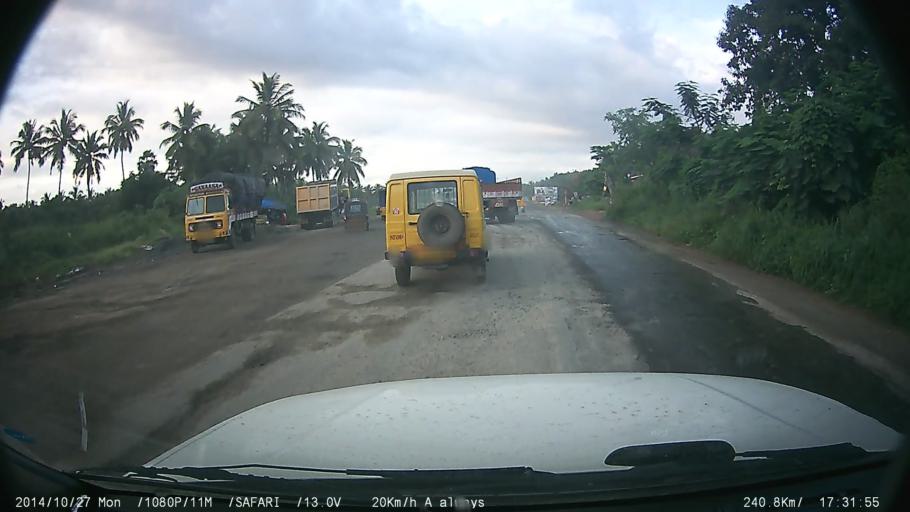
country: IN
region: Kerala
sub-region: Palakkad district
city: Palakkad
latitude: 10.6710
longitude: 76.5758
